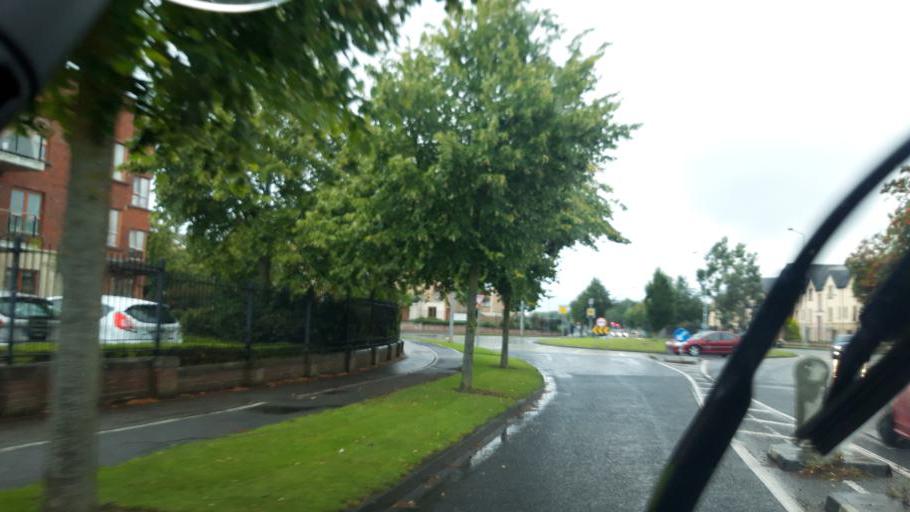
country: IE
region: Leinster
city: Hartstown
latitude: 53.3749
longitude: -6.4030
